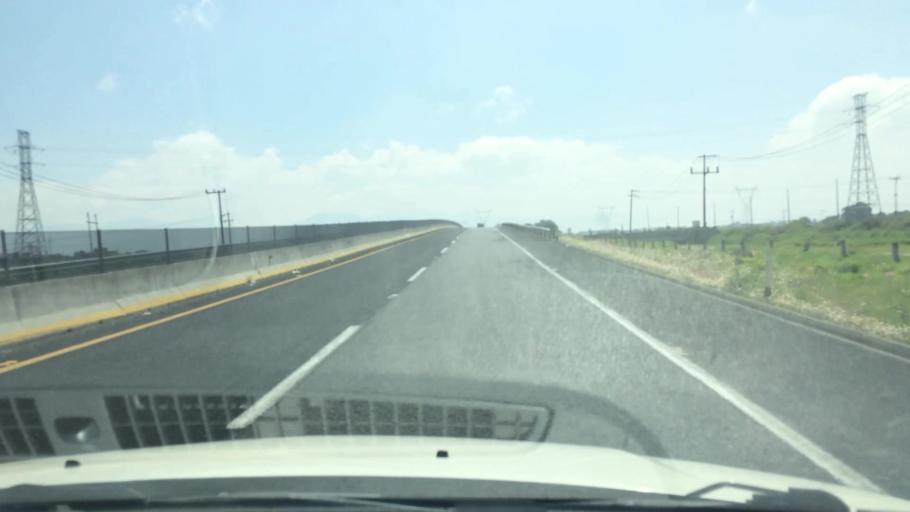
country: MX
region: Mexico
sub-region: Otzolotepec
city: La Y
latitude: 19.4057
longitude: -99.5956
